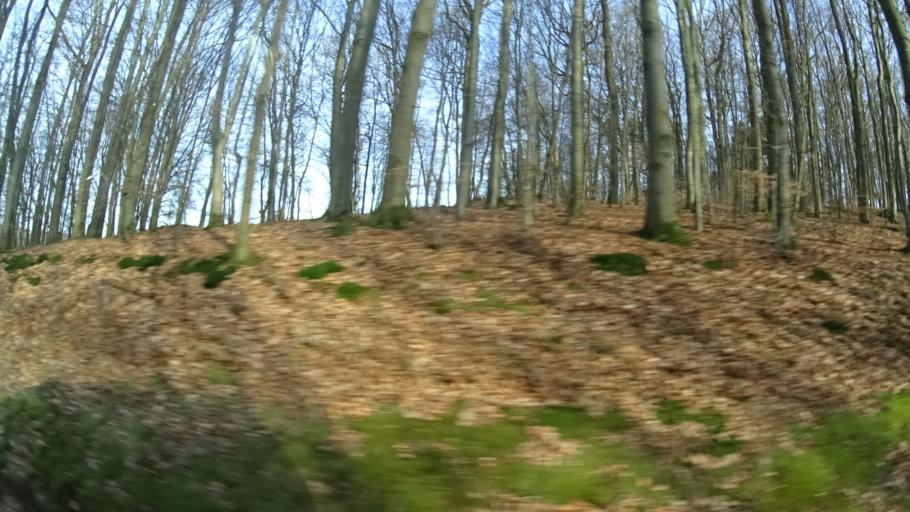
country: DE
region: Bavaria
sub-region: Regierungsbezirk Unterfranken
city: Bad Bruckenau
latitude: 50.3085
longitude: 9.7356
